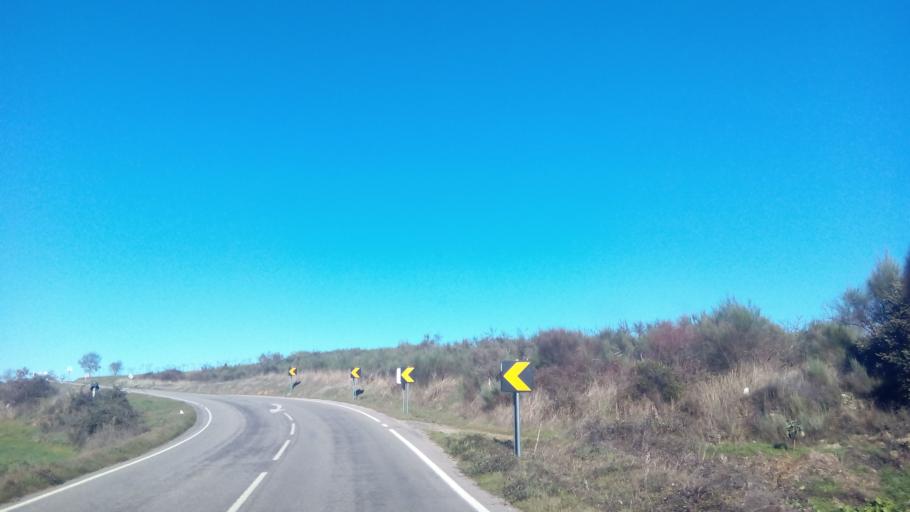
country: PT
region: Braganca
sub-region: Vimioso
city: Vimioso
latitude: 41.6635
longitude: -6.6136
